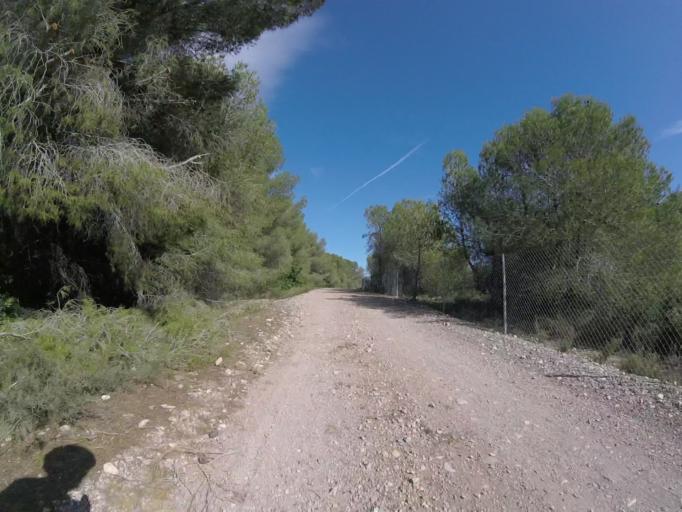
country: ES
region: Valencia
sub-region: Provincia de Castello
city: Santa Magdalena de Pulpis
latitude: 40.3856
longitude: 0.3445
